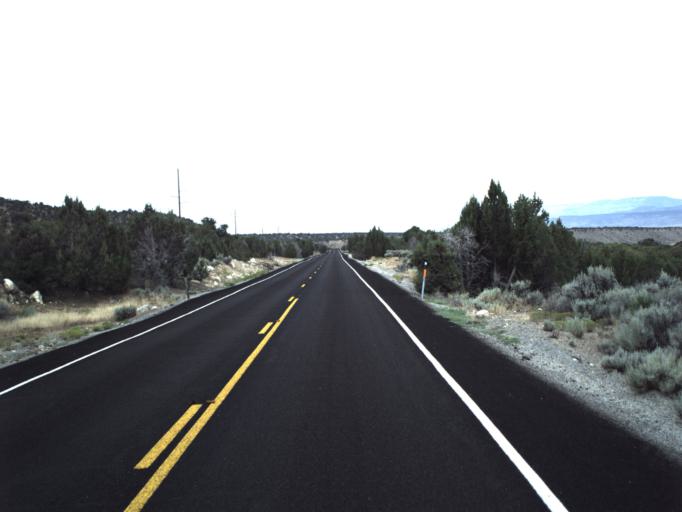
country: US
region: Utah
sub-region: Carbon County
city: East Carbon City
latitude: 39.5007
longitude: -110.3993
